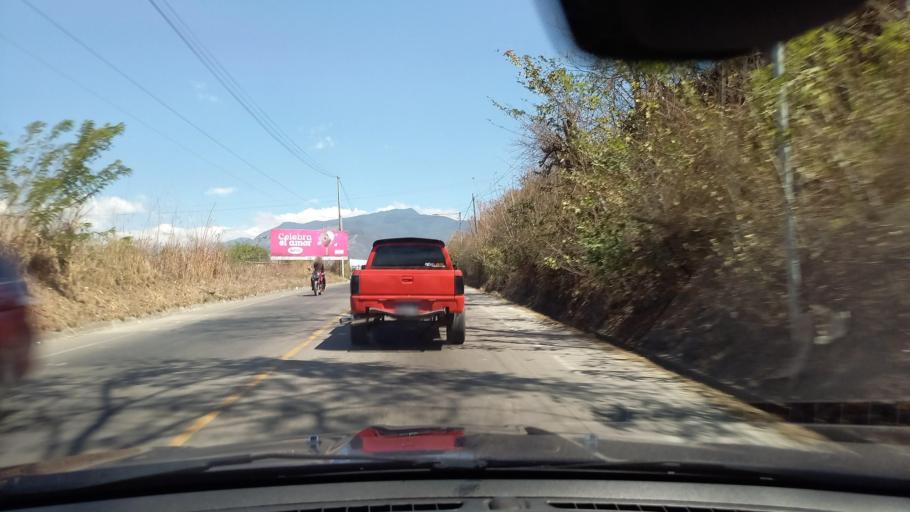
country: SV
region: Santa Ana
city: Metapan
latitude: 14.3146
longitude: -89.4485
